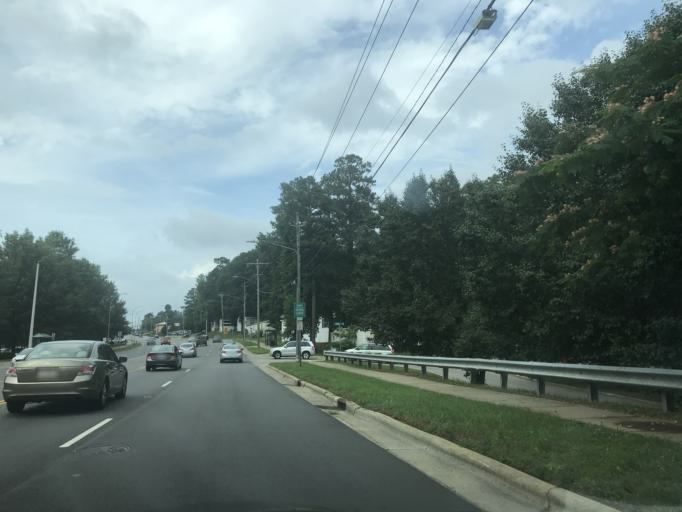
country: US
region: North Carolina
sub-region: Wake County
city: Cary
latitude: 35.7877
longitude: -78.7640
